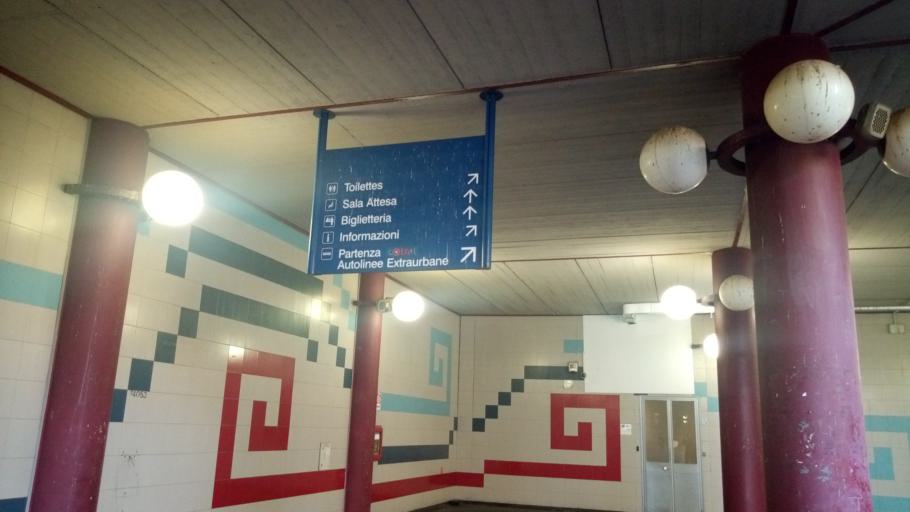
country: IT
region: Latium
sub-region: Citta metropolitana di Roma Capitale
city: Ciampino
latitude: 41.8429
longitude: 12.5859
